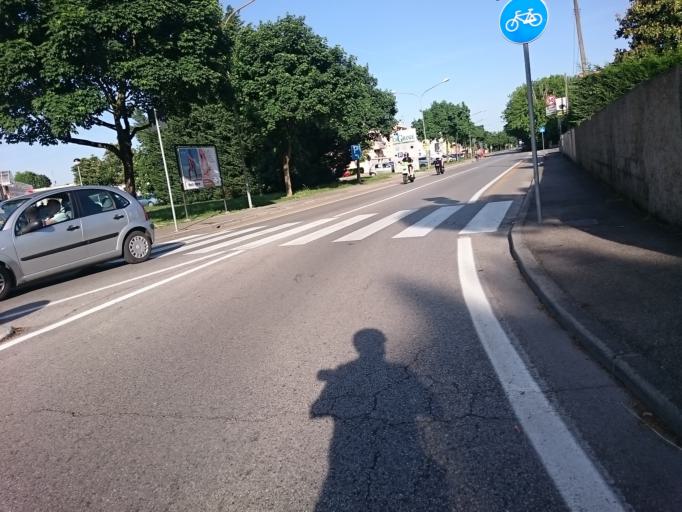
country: IT
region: Veneto
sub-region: Provincia di Padova
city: Abano Terme
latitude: 45.3591
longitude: 11.7951
